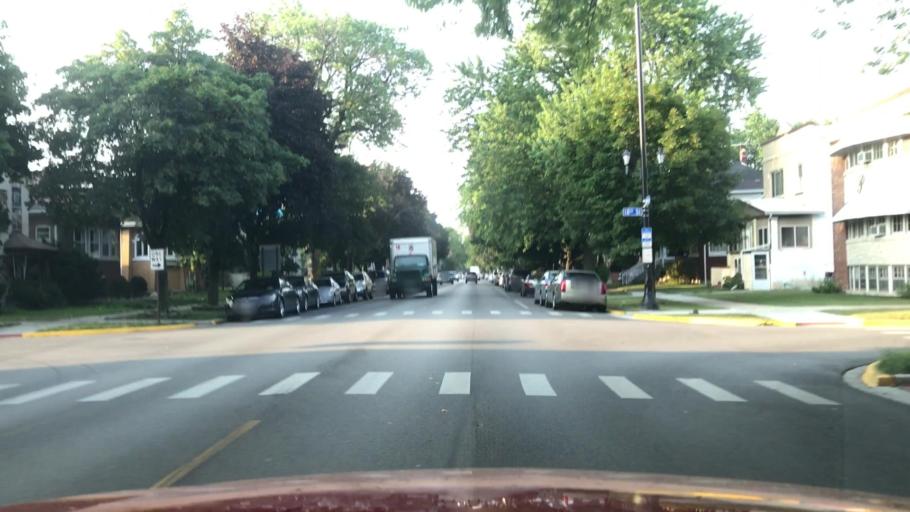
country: US
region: Illinois
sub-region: Cook County
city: Berwyn
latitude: 41.8565
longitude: -87.7739
